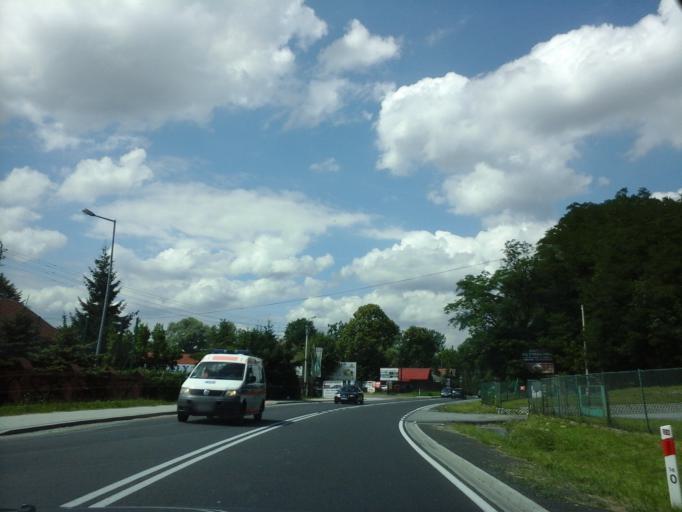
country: PL
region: Lesser Poland Voivodeship
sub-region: Powiat suski
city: Sucha Beskidzka
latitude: 49.7356
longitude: 19.6190
